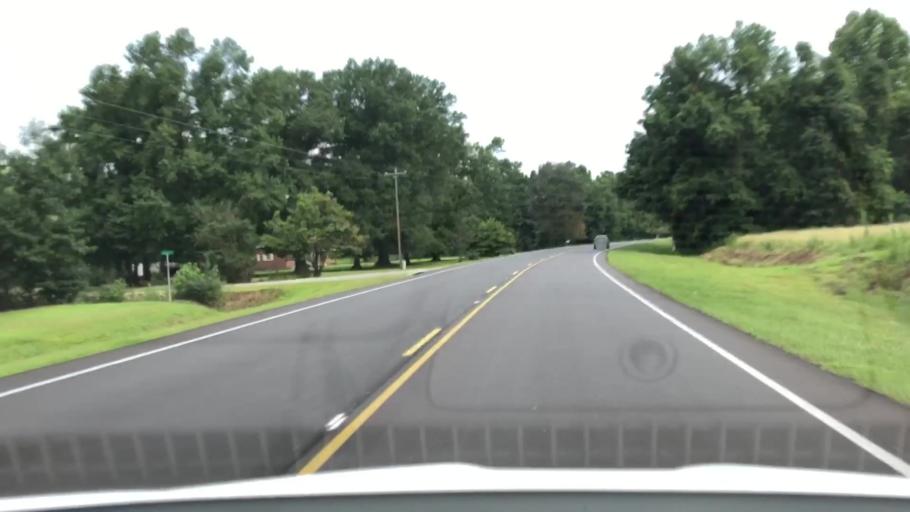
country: US
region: North Carolina
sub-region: Jones County
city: Maysville
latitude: 34.8867
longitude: -77.2125
